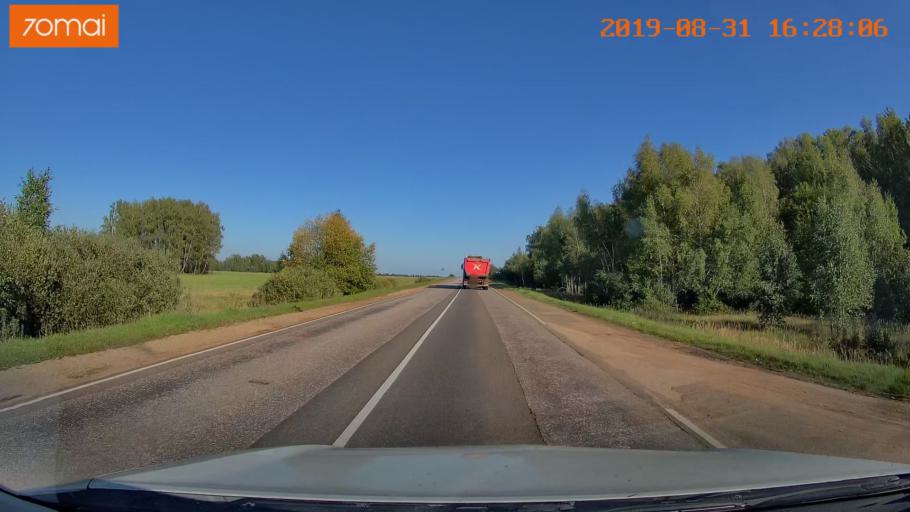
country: RU
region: Kaluga
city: Babynino
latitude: 54.5112
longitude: 35.7724
